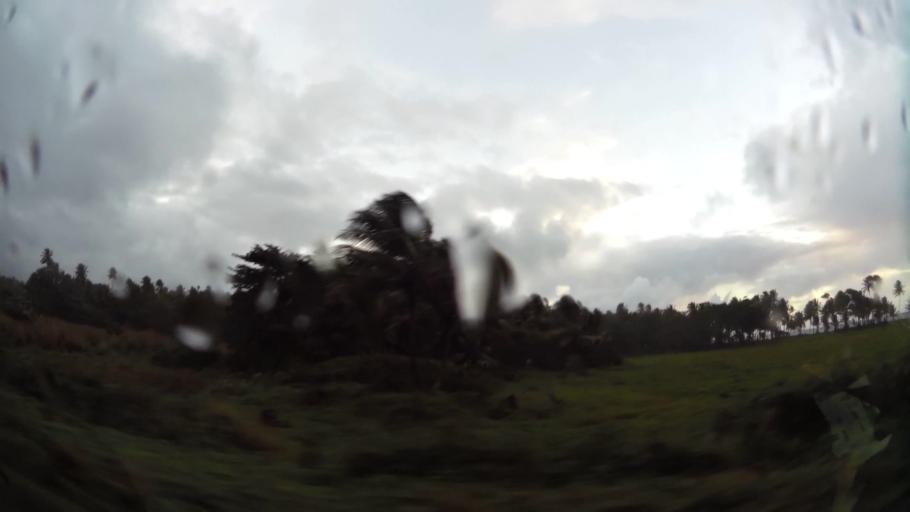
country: DM
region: Saint Andrew
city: Marigot
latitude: 15.5544
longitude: -61.2976
